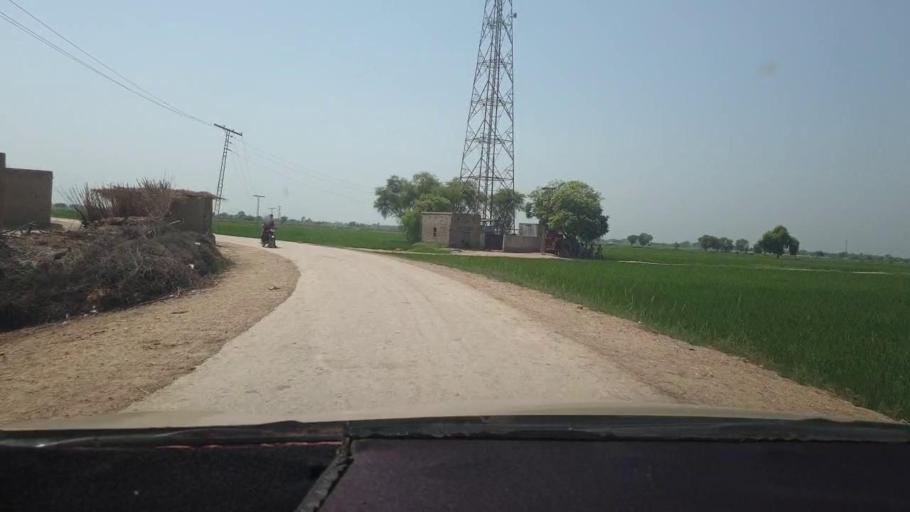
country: PK
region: Sindh
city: Miro Khan
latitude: 27.6619
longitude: 68.0792
